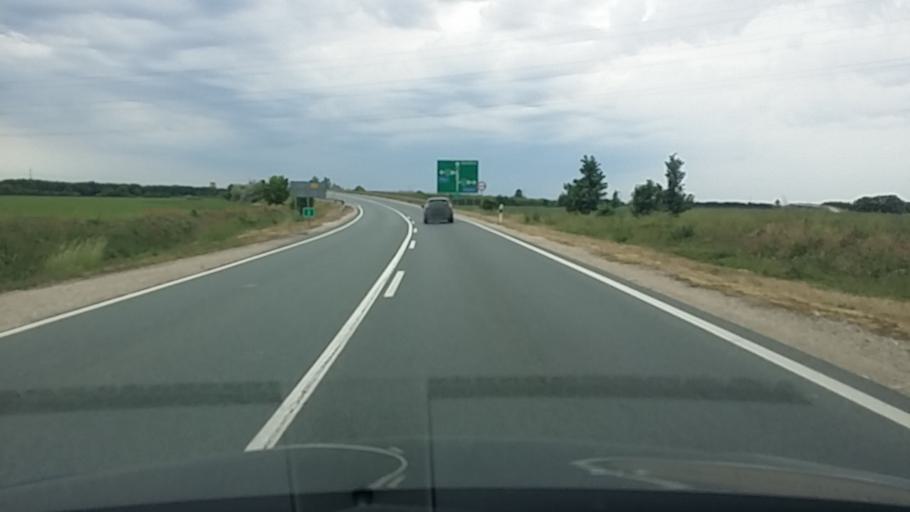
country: HU
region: Fejer
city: dunaujvaros
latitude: 46.9920
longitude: 18.8925
